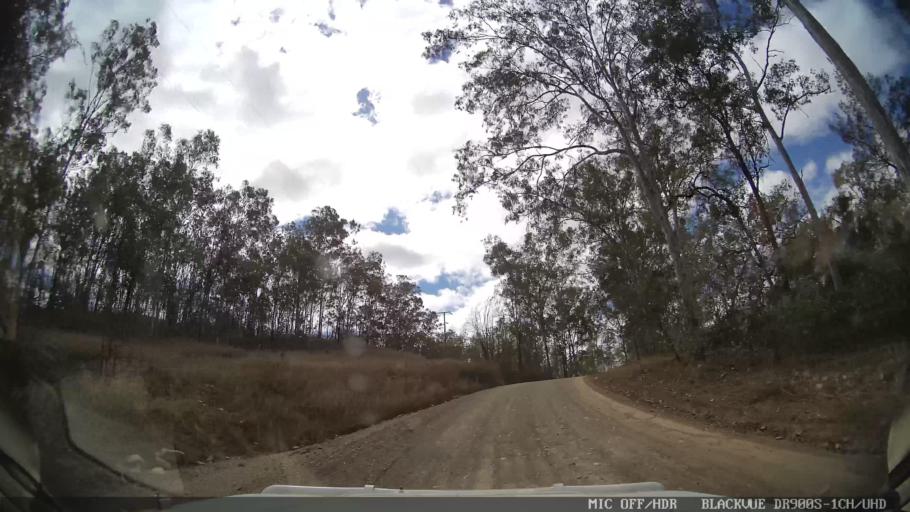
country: AU
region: Queensland
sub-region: Gladstone
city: Toolooa
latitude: -24.5528
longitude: 151.3364
